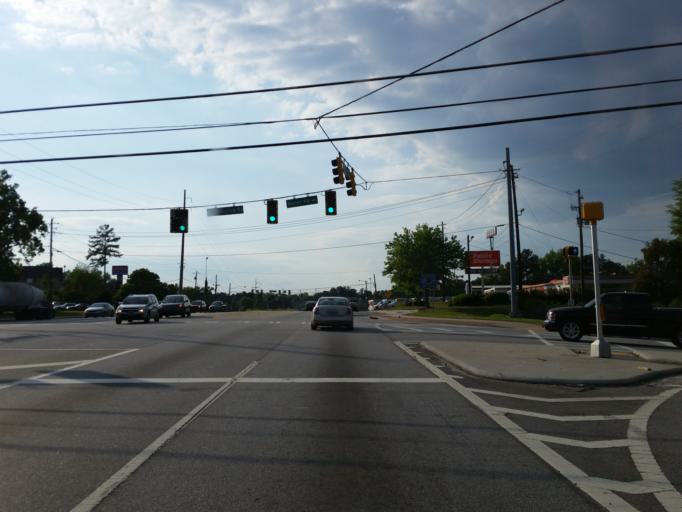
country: US
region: Georgia
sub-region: Cobb County
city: Vinings
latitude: 33.8234
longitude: -84.4871
